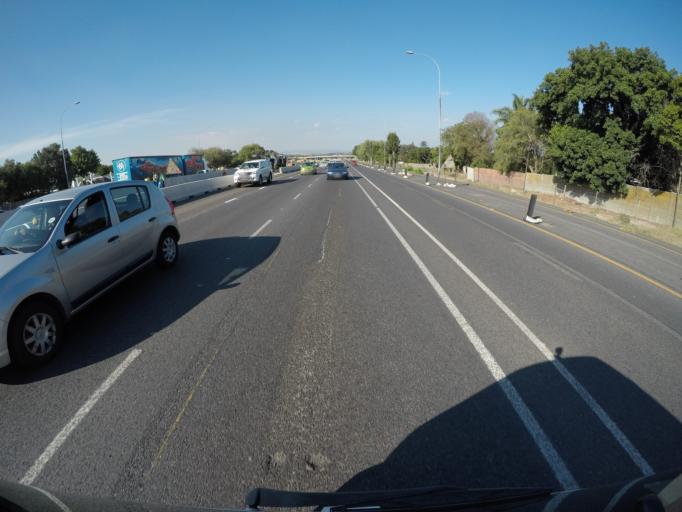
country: ZA
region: Western Cape
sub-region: City of Cape Town
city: Kraaifontein
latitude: -33.8794
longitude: 18.6535
